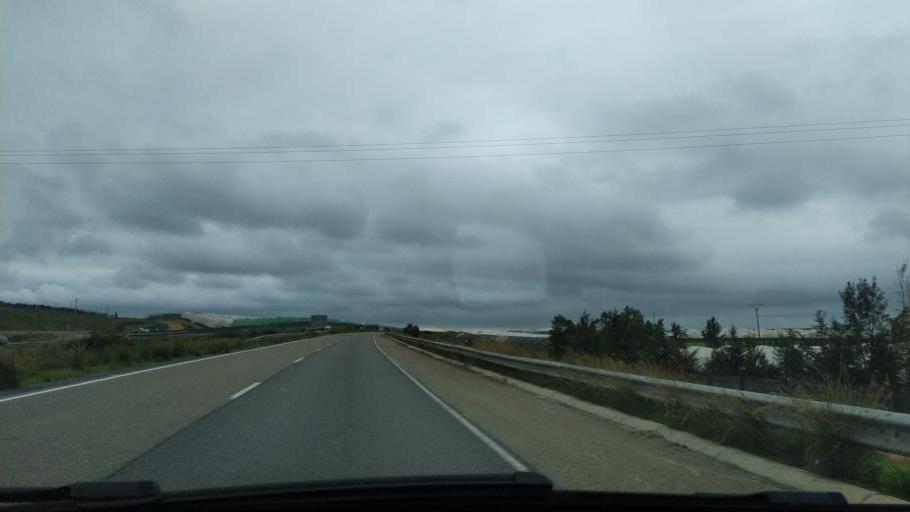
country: MA
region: Gharb-Chrarda-Beni Hssen
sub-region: Kenitra Province
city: Lalla Mimouna
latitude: 34.8395
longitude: -6.2277
